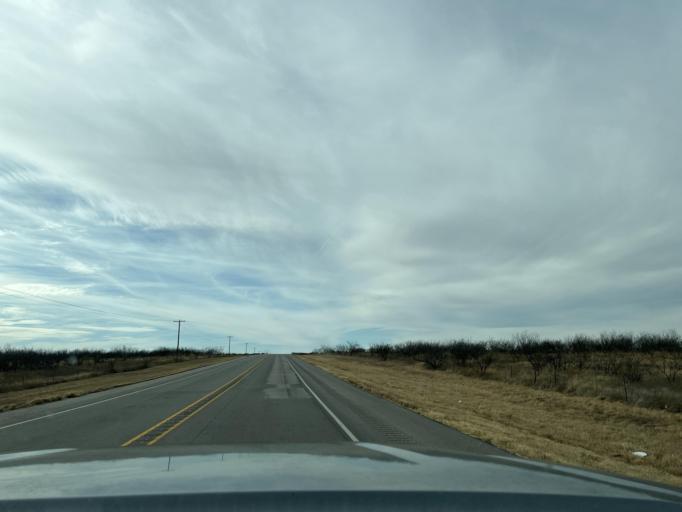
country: US
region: Texas
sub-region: Jones County
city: Anson
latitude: 32.7504
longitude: -99.6572
